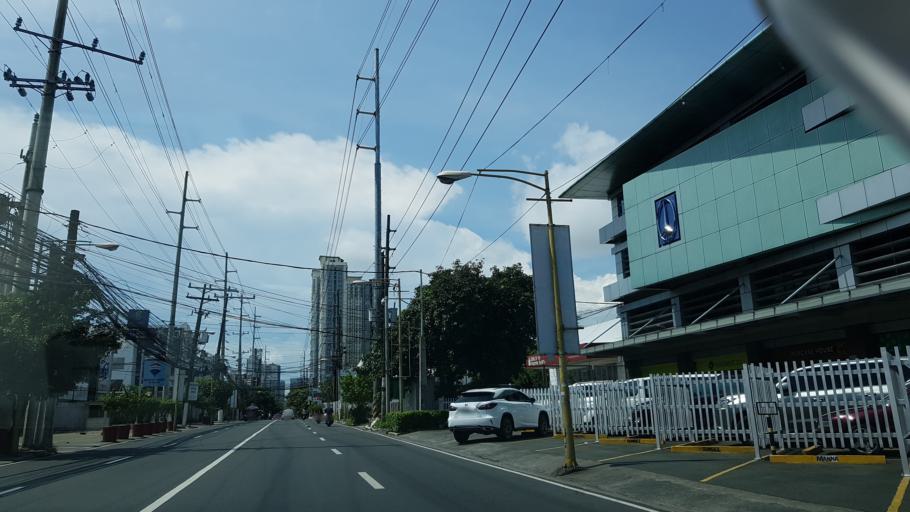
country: PH
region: Metro Manila
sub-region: Makati City
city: Makati City
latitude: 14.5375
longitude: 121.0204
